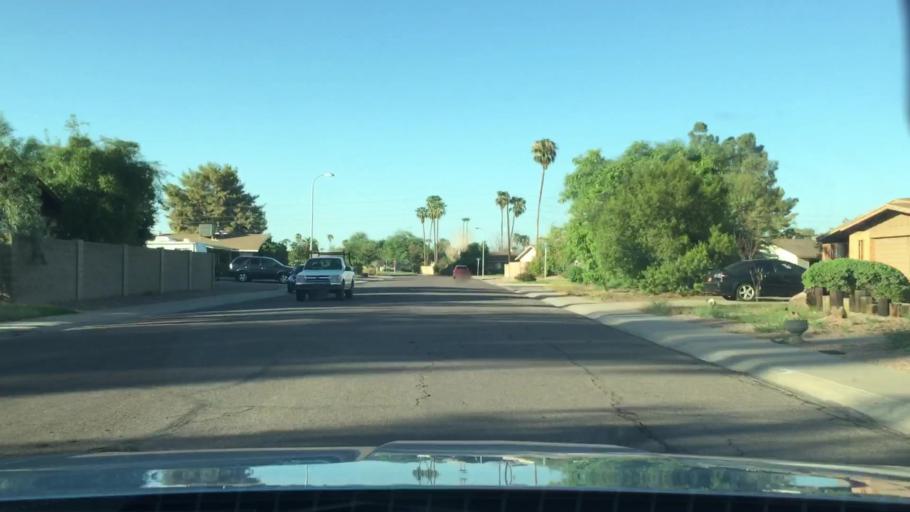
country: US
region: Arizona
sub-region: Maricopa County
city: Tempe
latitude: 33.3946
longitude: -111.9046
